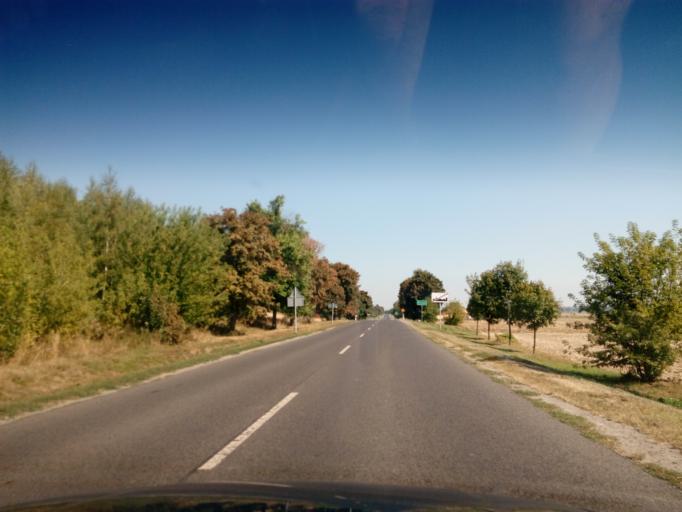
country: PL
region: Lublin Voivodeship
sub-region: Powiat hrubieszowski
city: Horodlo
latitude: 50.8439
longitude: 24.0463
